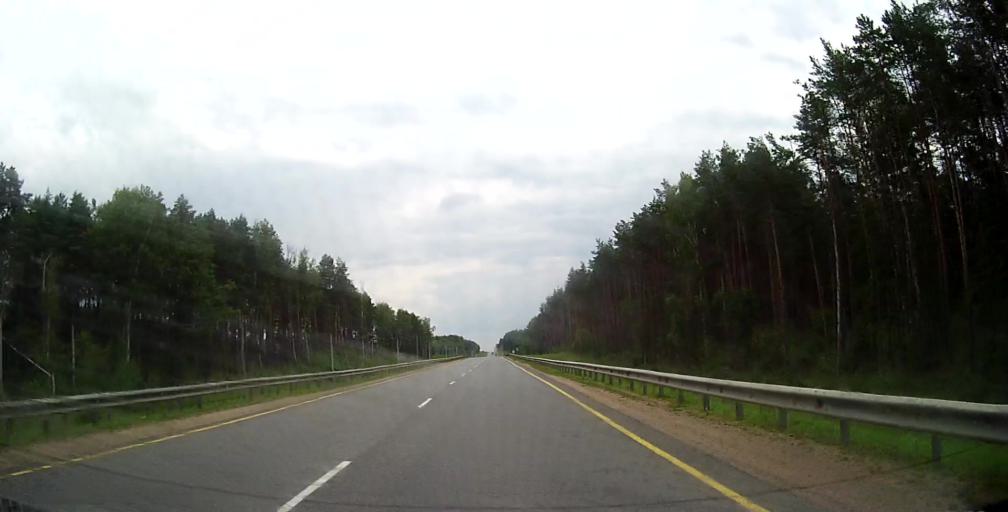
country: RU
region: Smolensk
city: Katyn'
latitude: 54.7703
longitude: 31.7597
